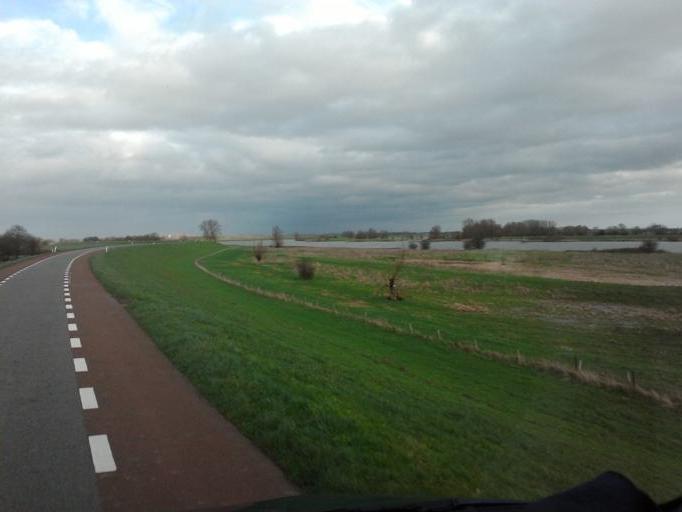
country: NL
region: Gelderland
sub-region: Gemeente Culemborg
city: Culemborg
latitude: 51.9706
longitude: 5.2215
